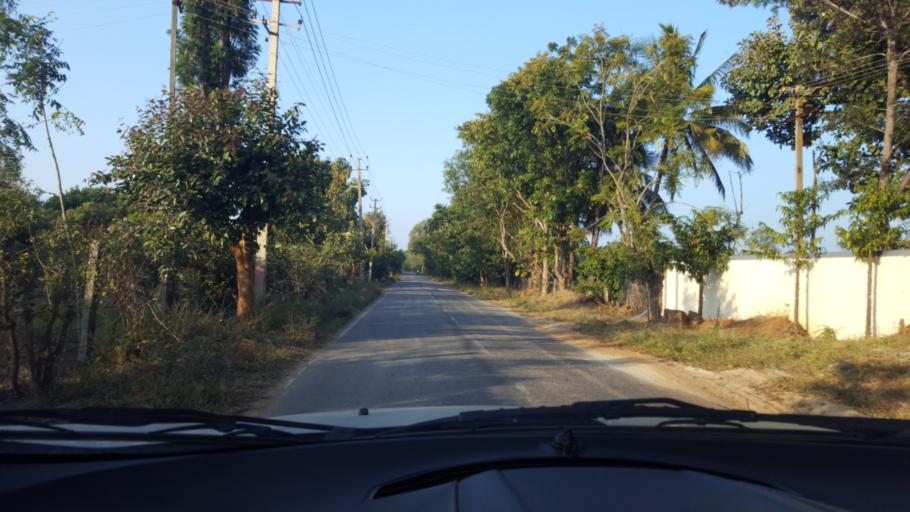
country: IN
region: Karnataka
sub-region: Bangalore Urban
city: Yelahanka
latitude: 13.1736
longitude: 77.5990
